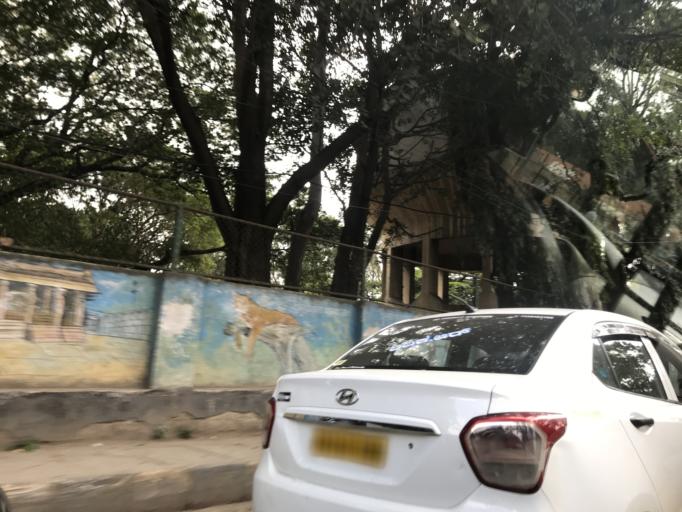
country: IN
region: Karnataka
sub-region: Bangalore Urban
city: Bangalore
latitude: 12.9625
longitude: 77.5602
